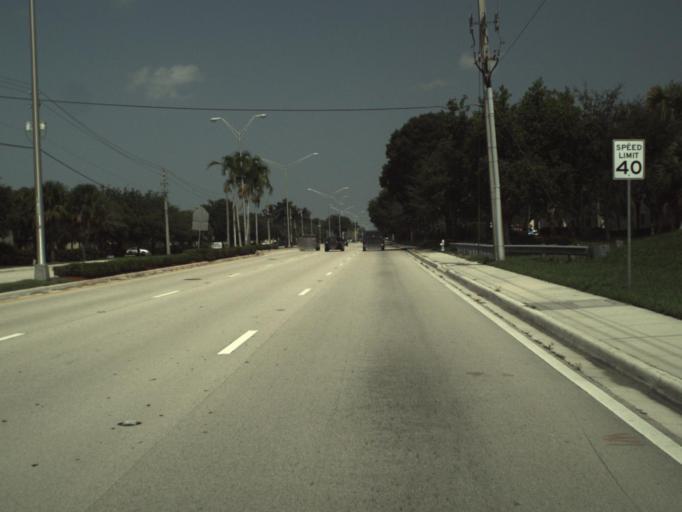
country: US
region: Florida
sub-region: Broward County
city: Coral Springs
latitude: 26.2728
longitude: -80.2903
